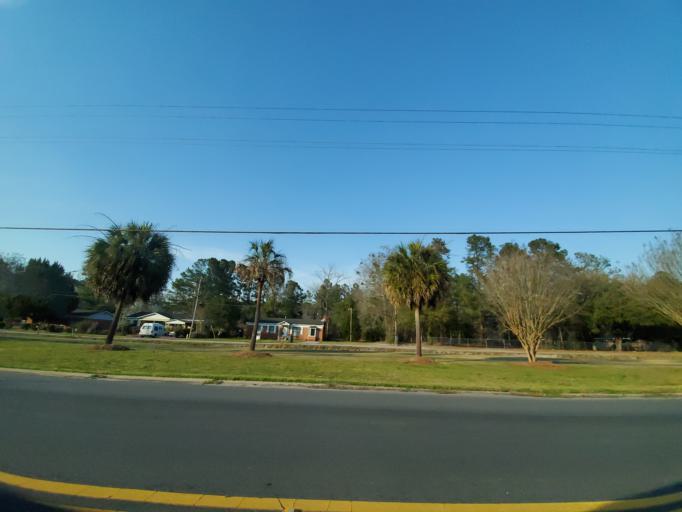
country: US
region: South Carolina
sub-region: Bamberg County
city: Bamberg
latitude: 33.3001
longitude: -81.0464
